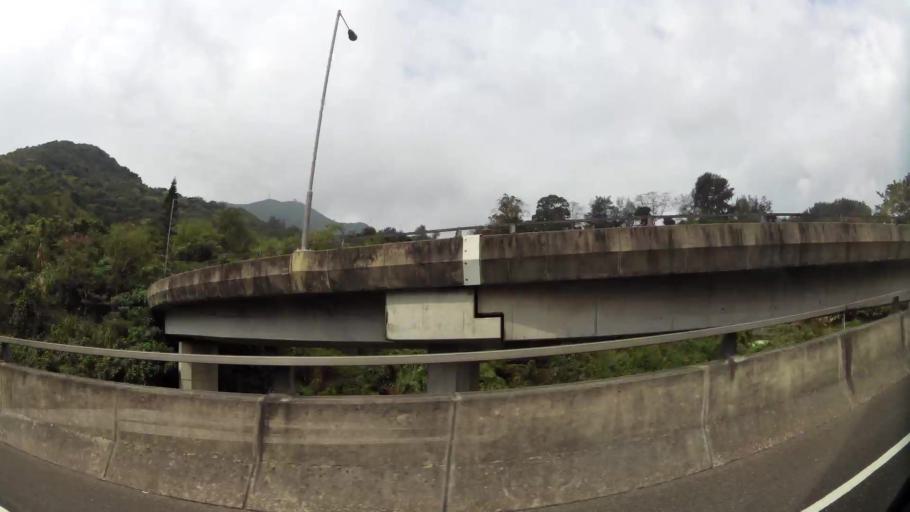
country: HK
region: Wanchai
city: Wan Chai
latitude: 22.2776
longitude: 114.2369
